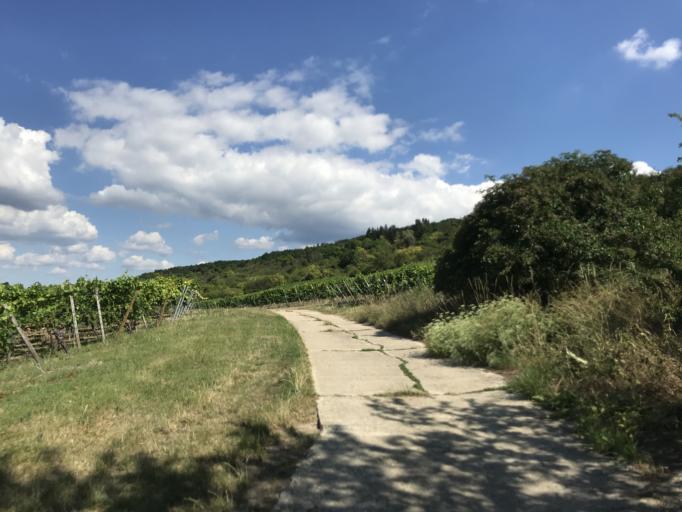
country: DE
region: Rheinland-Pfalz
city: Appenheim
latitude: 49.9398
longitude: 8.0357
